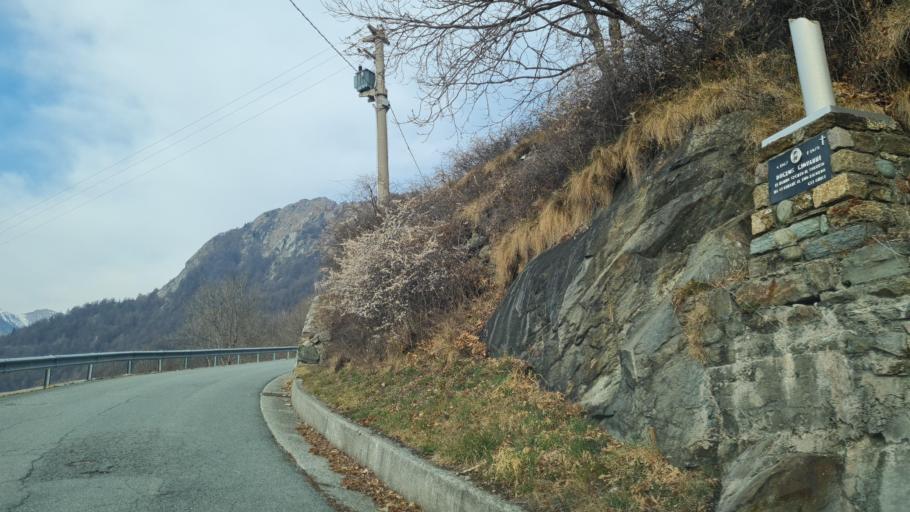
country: IT
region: Aosta Valley
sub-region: Valle d'Aosta
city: Pont-Bozet
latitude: 45.6188
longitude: 7.7110
